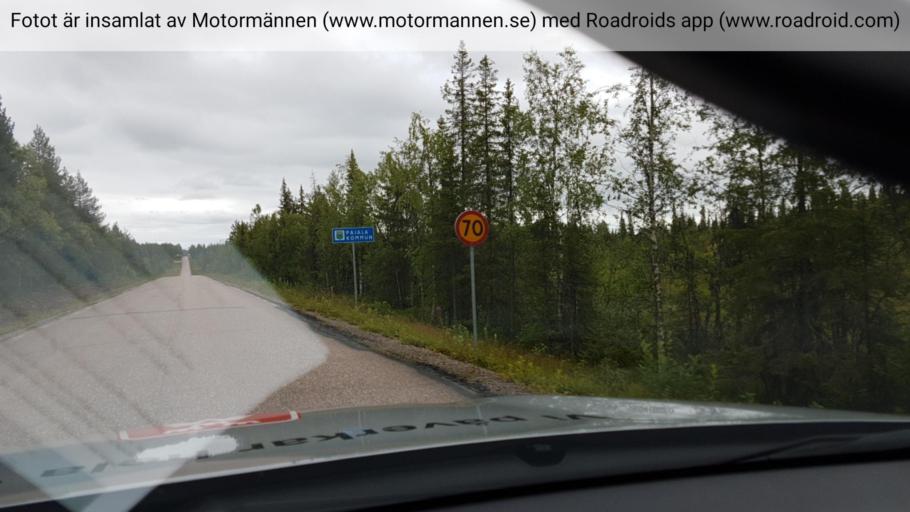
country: SE
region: Norrbotten
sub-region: Overkalix Kommun
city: OEverkalix
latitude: 67.0448
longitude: 22.0746
